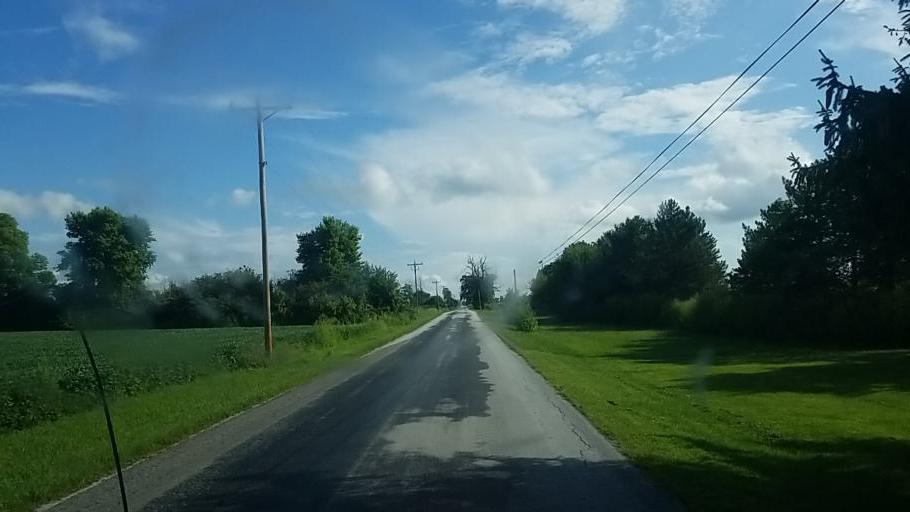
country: US
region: Ohio
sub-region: Hardin County
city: Kenton
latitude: 40.6761
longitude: -83.5380
